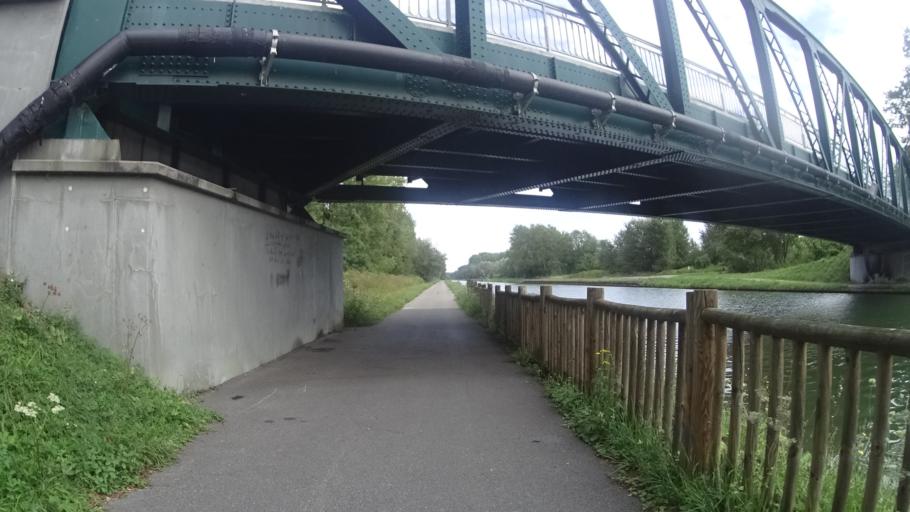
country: FR
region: Picardie
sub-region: Departement de l'Oise
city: Noyon
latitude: 49.5690
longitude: 3.0526
